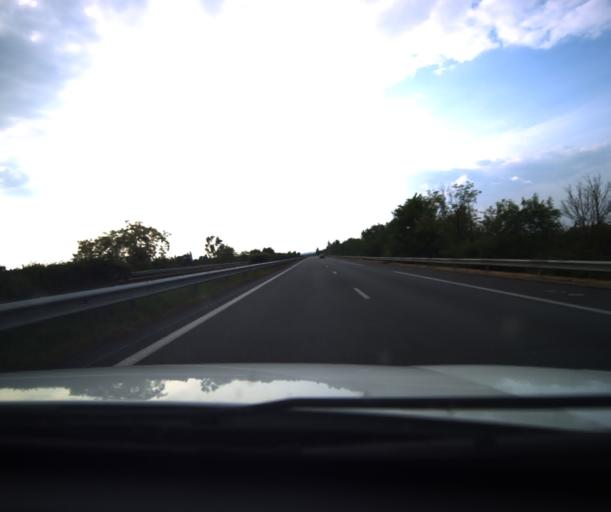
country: FR
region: Midi-Pyrenees
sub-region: Departement du Tarn-et-Garonne
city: Saint-Porquier
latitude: 44.0400
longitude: 1.1515
